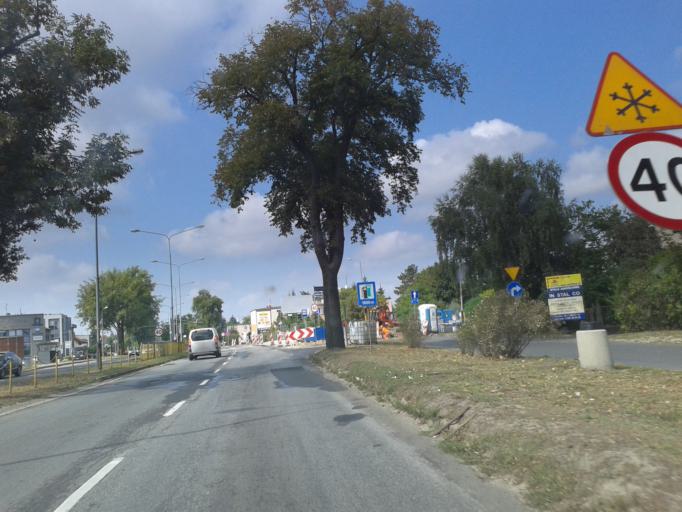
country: PL
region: Greater Poland Voivodeship
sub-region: Powiat poznanski
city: Suchy Las
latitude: 52.4260
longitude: 16.8609
